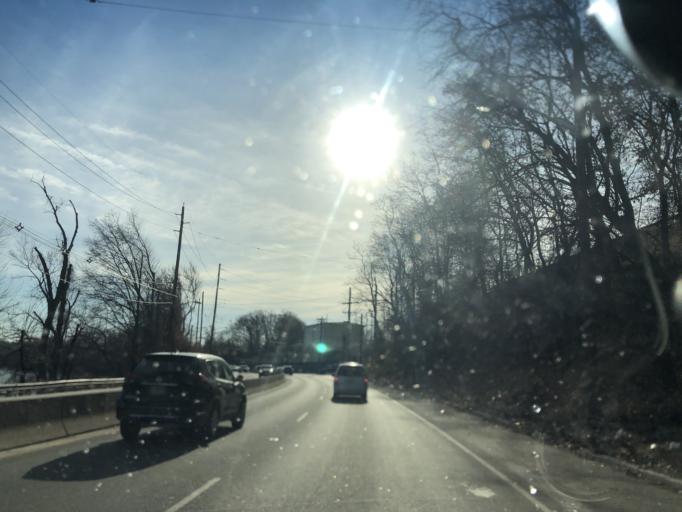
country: US
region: New Jersey
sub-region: Bergen County
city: Fair Lawn
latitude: 40.9304
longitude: -74.1428
